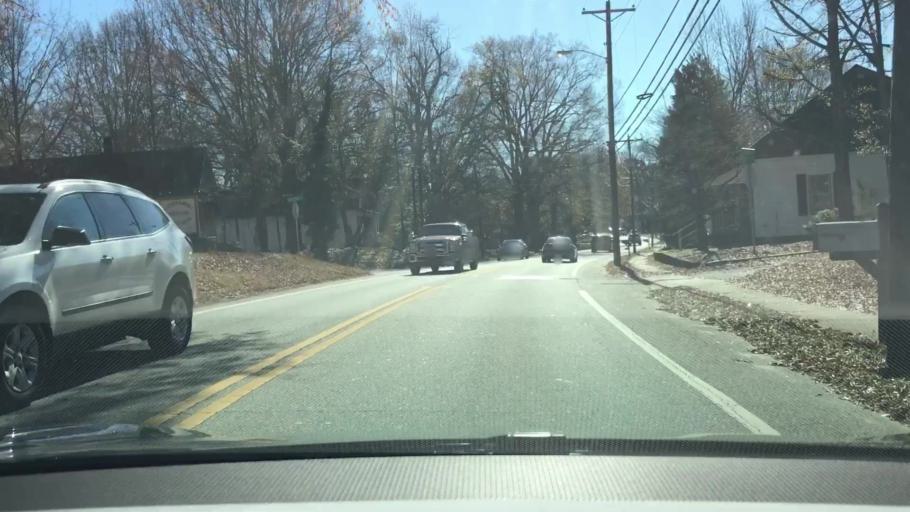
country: US
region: Georgia
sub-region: Walton County
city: Monroe
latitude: 33.7847
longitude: -83.7087
